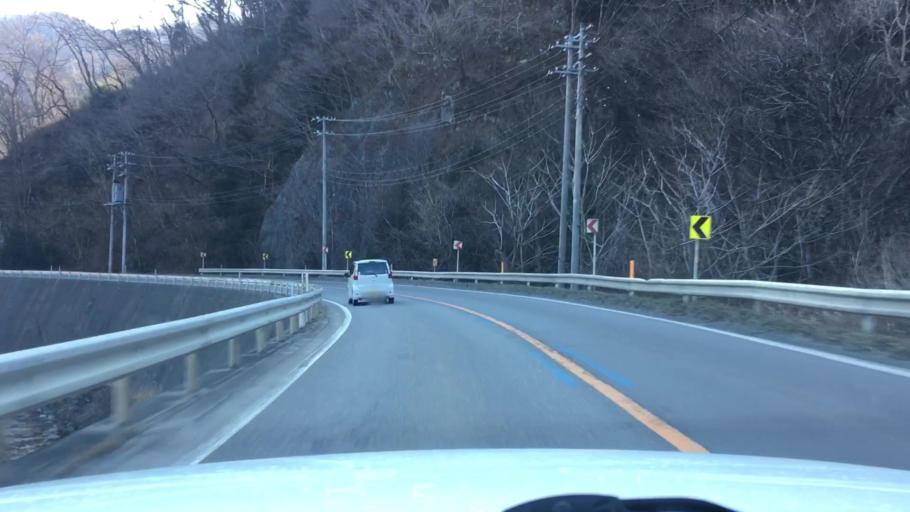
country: JP
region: Iwate
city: Miyako
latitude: 39.6063
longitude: 141.7720
